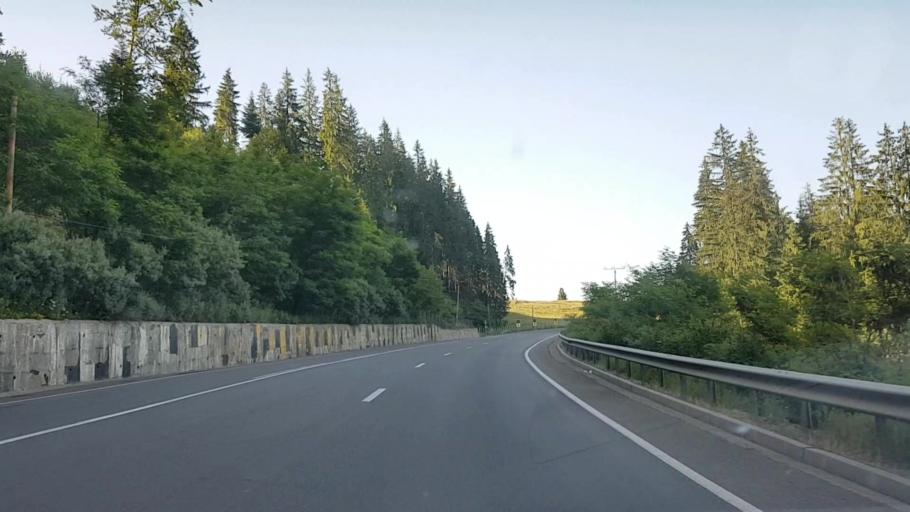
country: RO
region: Bistrita-Nasaud
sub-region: Comuna Lunca Ilvei
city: Lunca Ilvei
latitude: 47.2282
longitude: 24.9763
